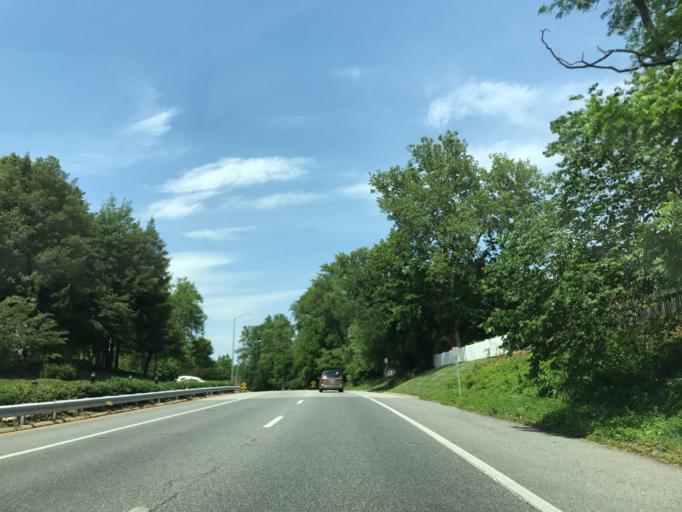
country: US
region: Maryland
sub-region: Anne Arundel County
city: Naval Academy
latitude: 38.9980
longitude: -76.4815
